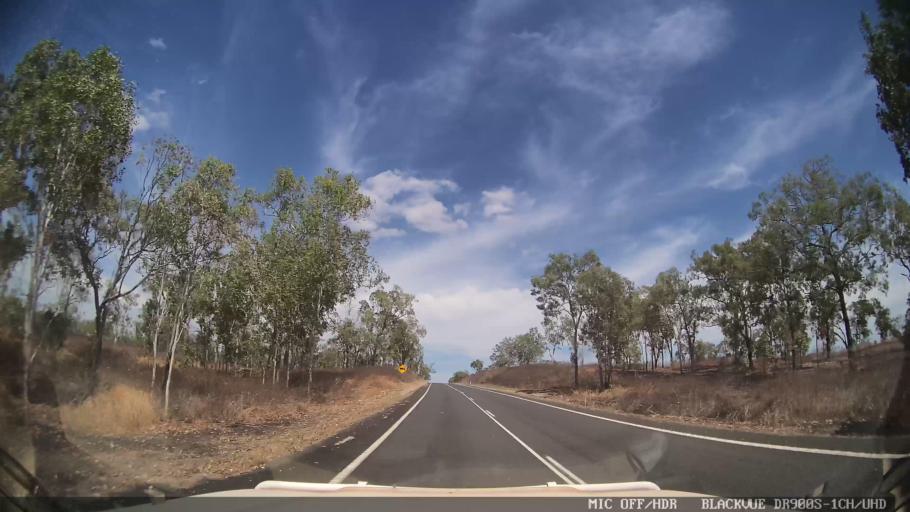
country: AU
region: Queensland
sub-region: Cook
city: Cooktown
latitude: -15.8042
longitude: 144.9214
